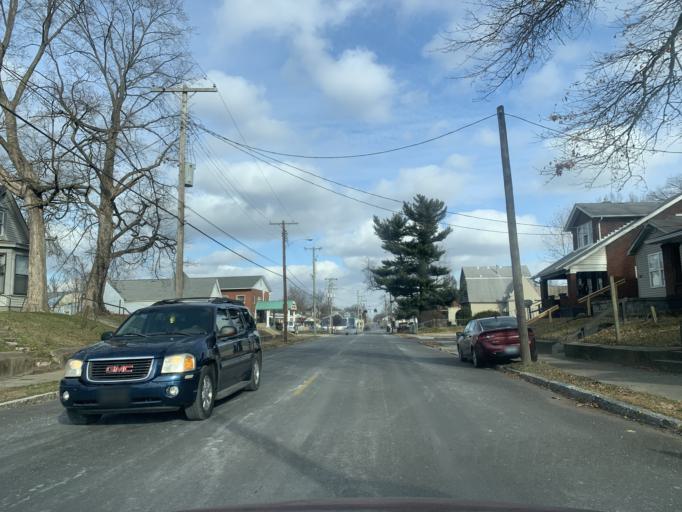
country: US
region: Kentucky
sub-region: Jefferson County
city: Louisville
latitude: 38.2365
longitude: -85.7964
